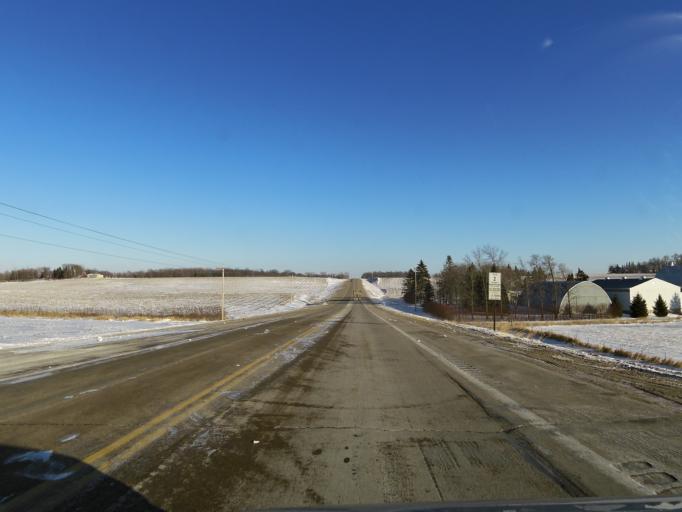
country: US
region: Minnesota
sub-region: Le Sueur County
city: Montgomery
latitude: 44.4861
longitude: -93.5242
